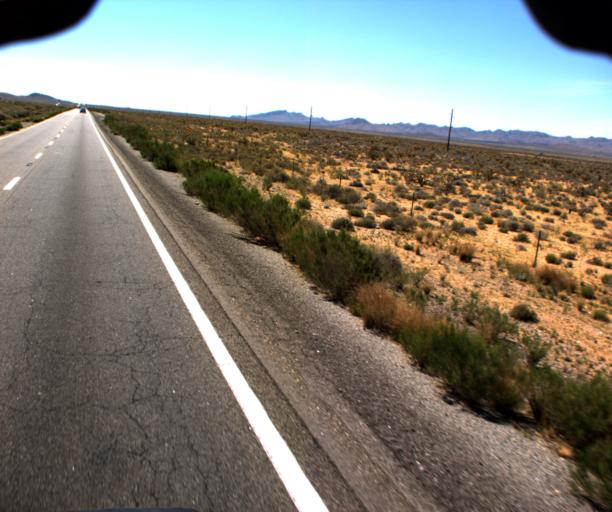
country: US
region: Arizona
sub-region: Mohave County
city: Dolan Springs
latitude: 35.4841
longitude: -114.3212
